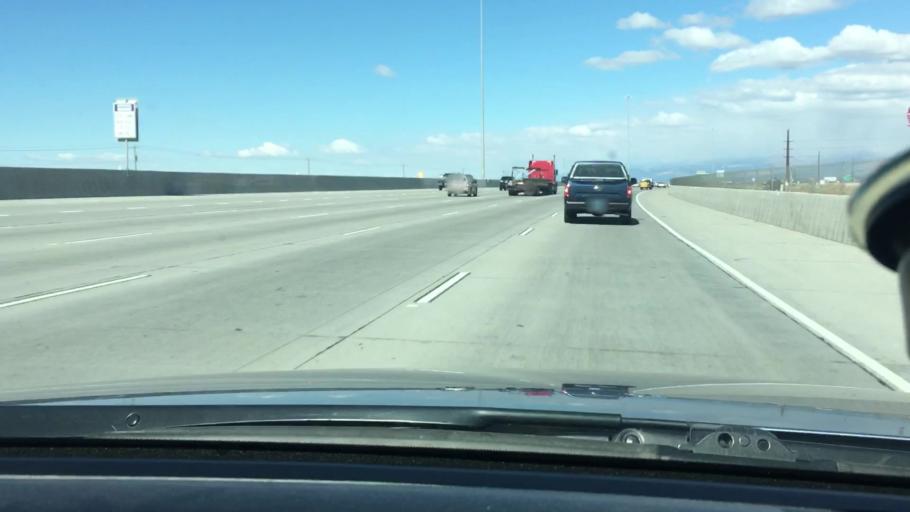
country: US
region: Utah
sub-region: Salt Lake County
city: Bluffdale
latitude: 40.4595
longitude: -111.9143
